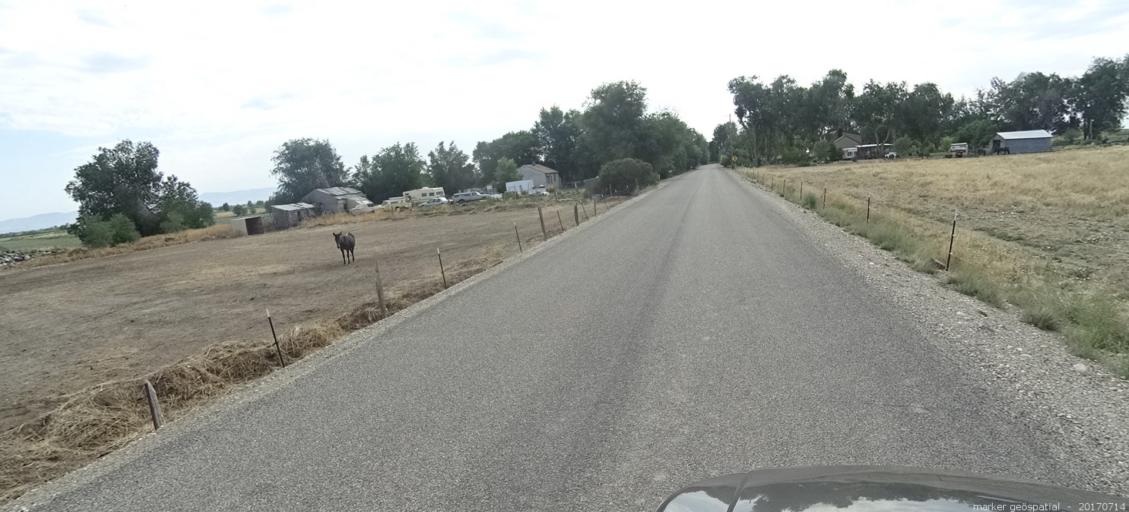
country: US
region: Idaho
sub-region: Ada County
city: Kuna
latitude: 43.4593
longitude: -116.3820
